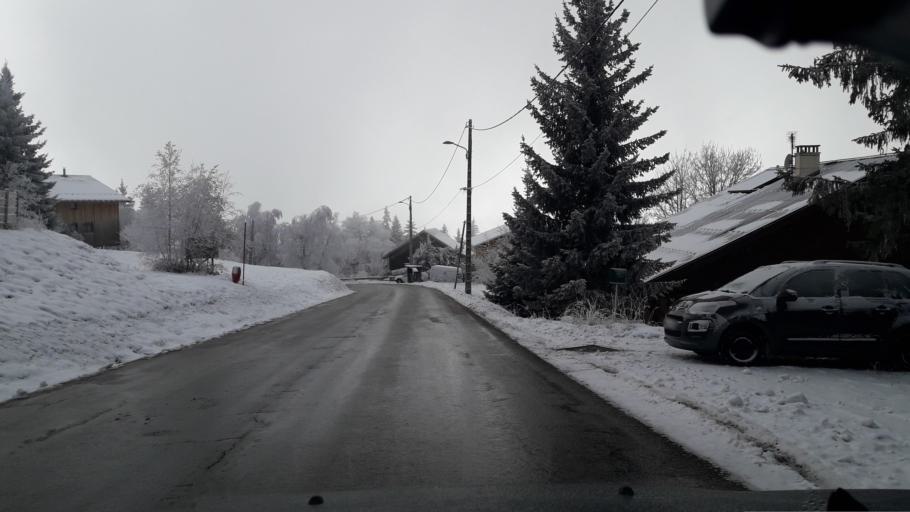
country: FR
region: Rhone-Alpes
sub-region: Departement de l'Isere
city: Allevard
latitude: 45.3925
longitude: 6.1057
